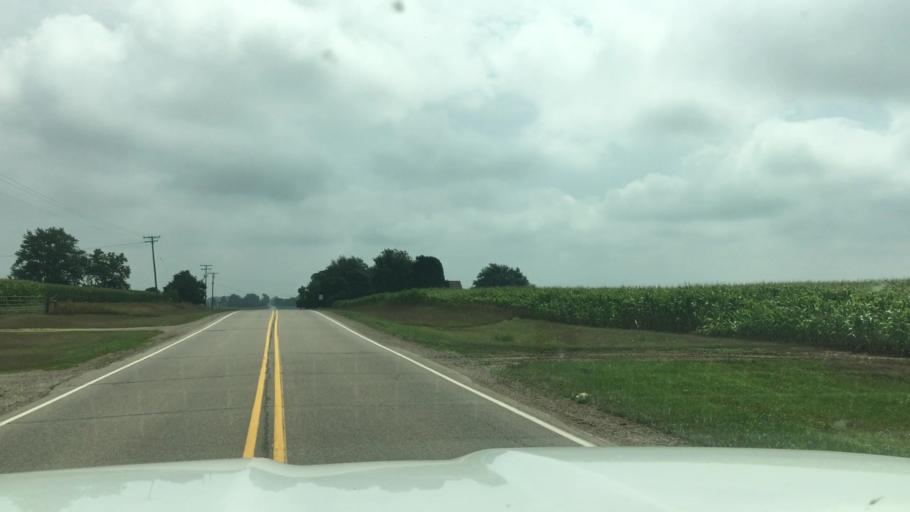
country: US
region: Michigan
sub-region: Sanilac County
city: Marlette
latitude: 43.3301
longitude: -82.9772
